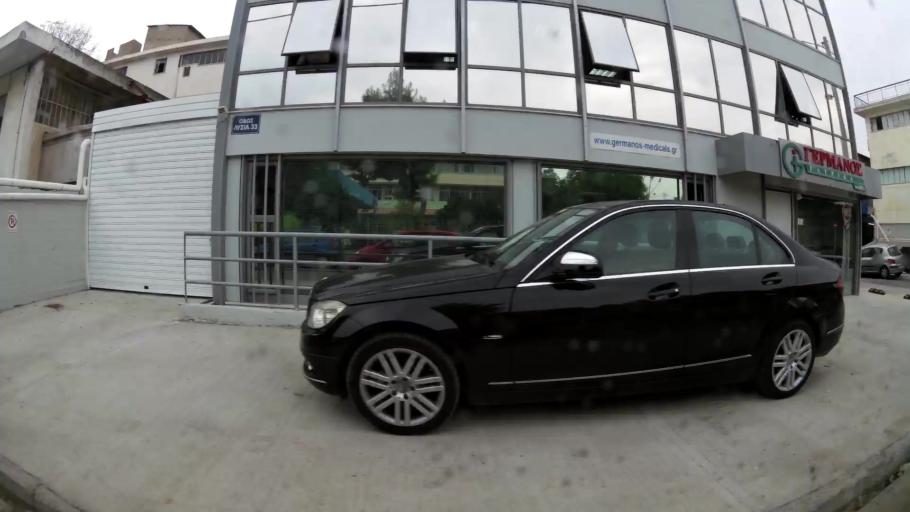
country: GR
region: Attica
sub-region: Nomarchia Athinas
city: Peristeri
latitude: 38.0087
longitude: 23.7094
